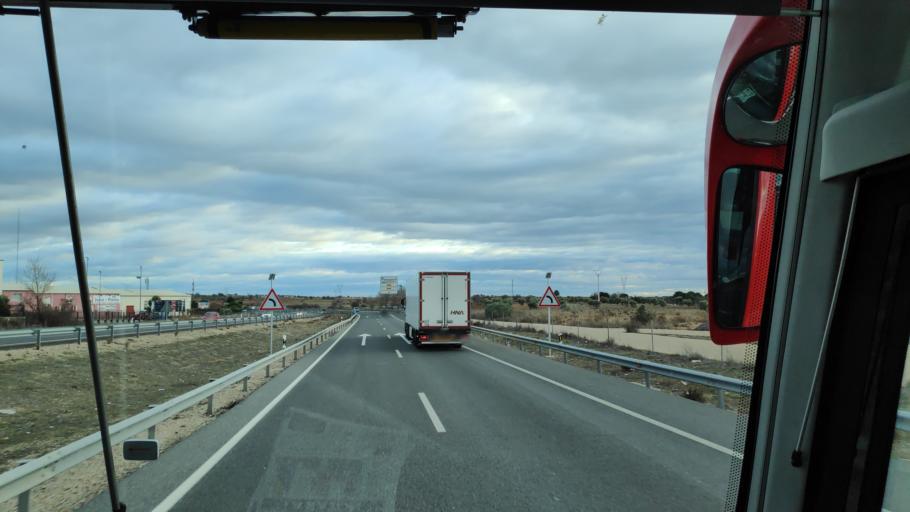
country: ES
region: Madrid
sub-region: Provincia de Madrid
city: Villarejo de Salvanes
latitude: 40.1771
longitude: -3.2960
